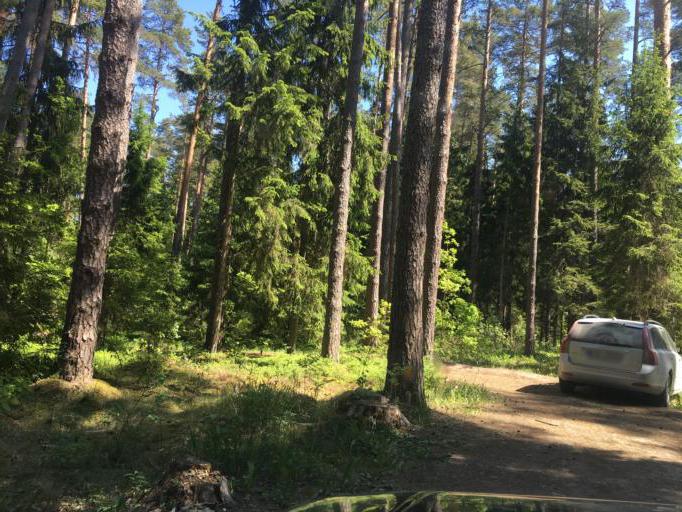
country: LV
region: Talsu Rajons
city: Valdemarpils
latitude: 57.4316
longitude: 22.6911
